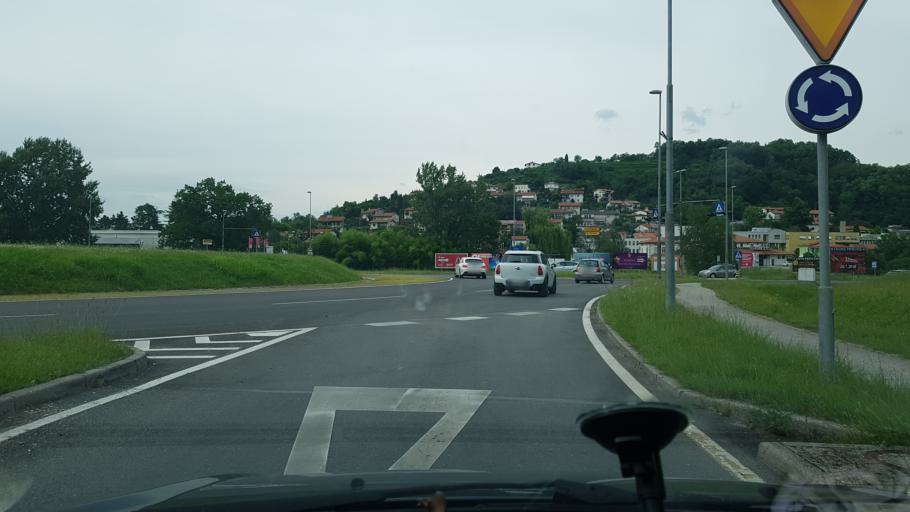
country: SI
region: Sempeter-Vrtojba
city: Sempeter pri Gorici
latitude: 45.9397
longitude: 13.6384
